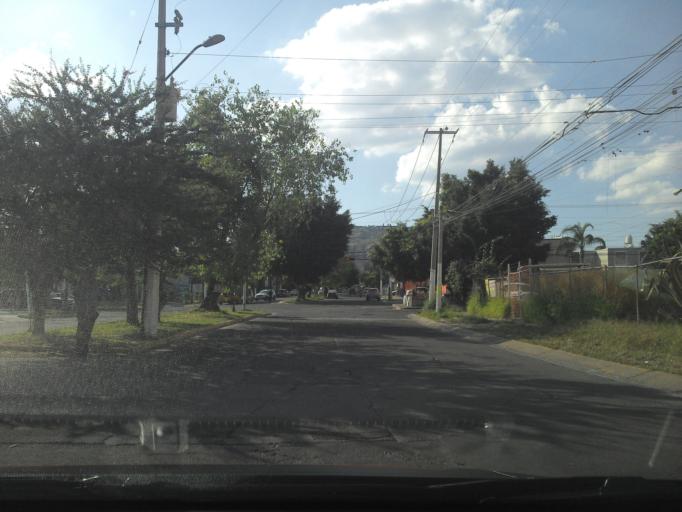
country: MX
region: Jalisco
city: Guadalajara
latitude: 20.6523
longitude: -103.4408
